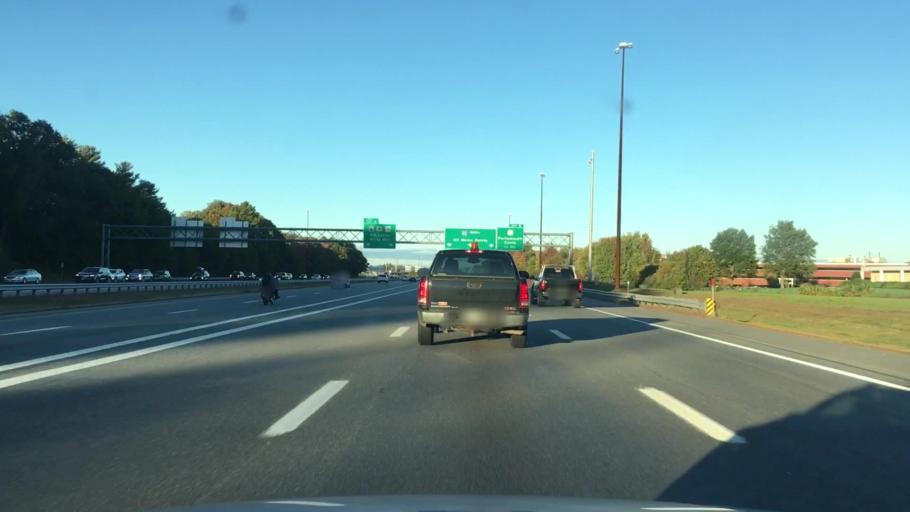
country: US
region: New Hampshire
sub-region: Rockingham County
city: Portsmouth
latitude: 43.0612
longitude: -70.7990
